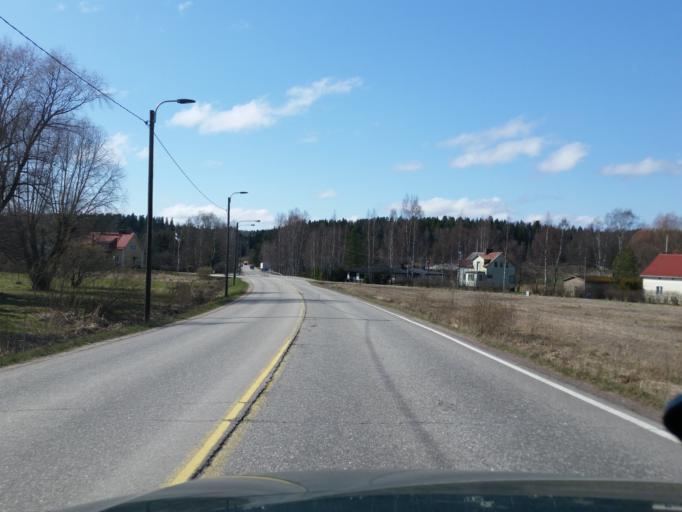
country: FI
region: Uusimaa
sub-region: Helsinki
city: Vihti
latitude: 60.4208
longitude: 24.3173
